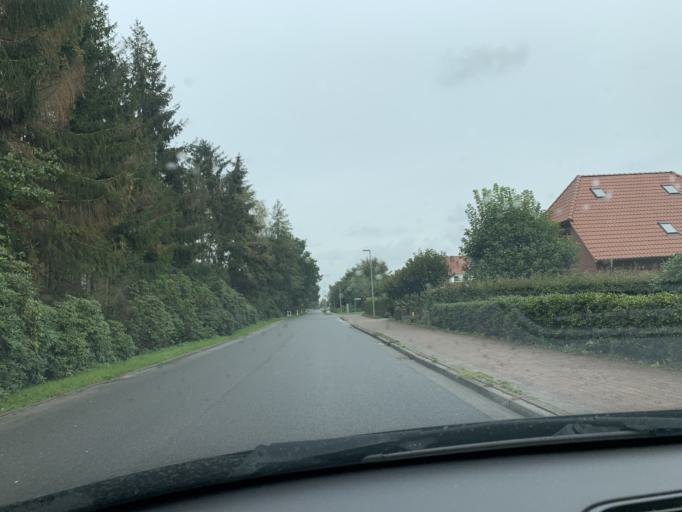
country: DE
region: Lower Saxony
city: Edewecht
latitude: 53.1249
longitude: 8.0832
